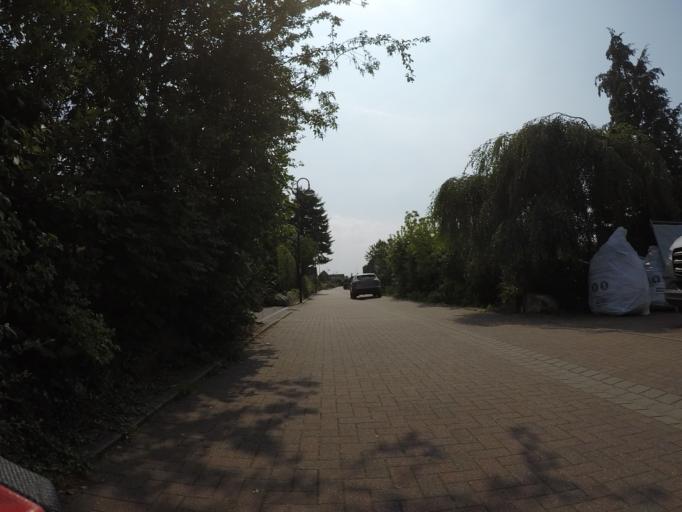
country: DE
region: Schleswig-Holstein
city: Kisdorf
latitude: 53.8074
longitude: 10.0107
